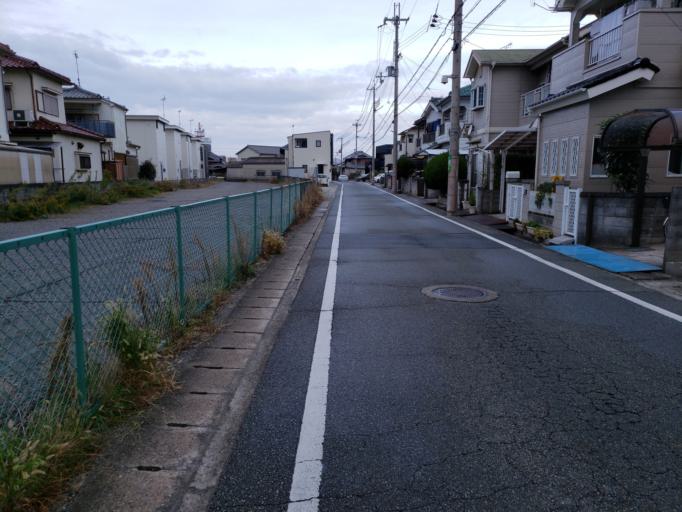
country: JP
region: Hyogo
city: Kakogawacho-honmachi
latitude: 34.7560
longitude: 134.8465
